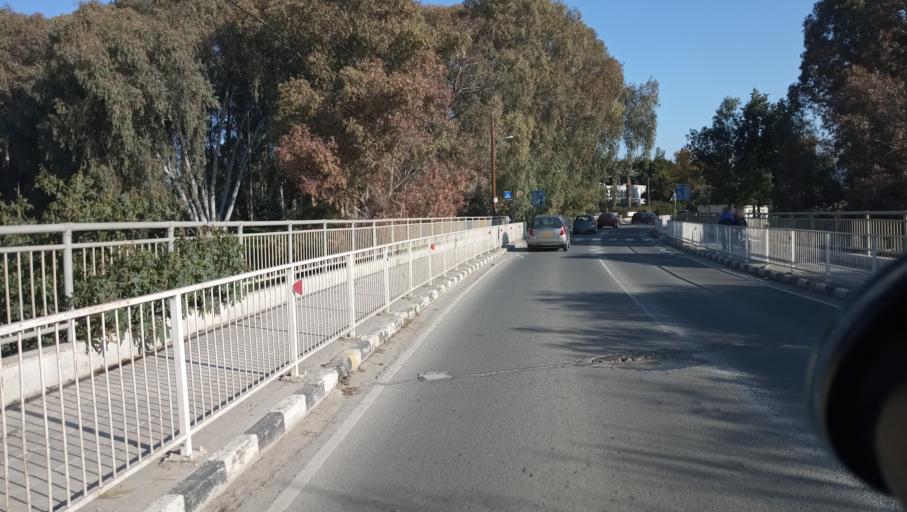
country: CY
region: Lefkosia
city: Nicosia
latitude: 35.1387
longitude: 33.3290
